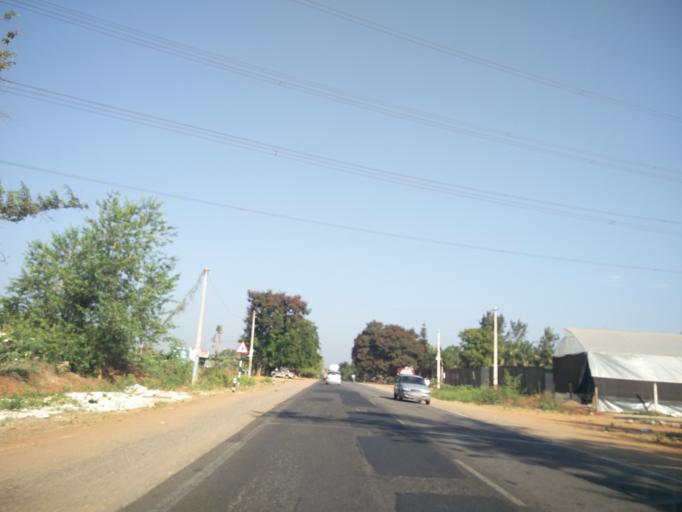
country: IN
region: Karnataka
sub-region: Tumkur
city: Gubbi
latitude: 13.3129
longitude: 76.9141
